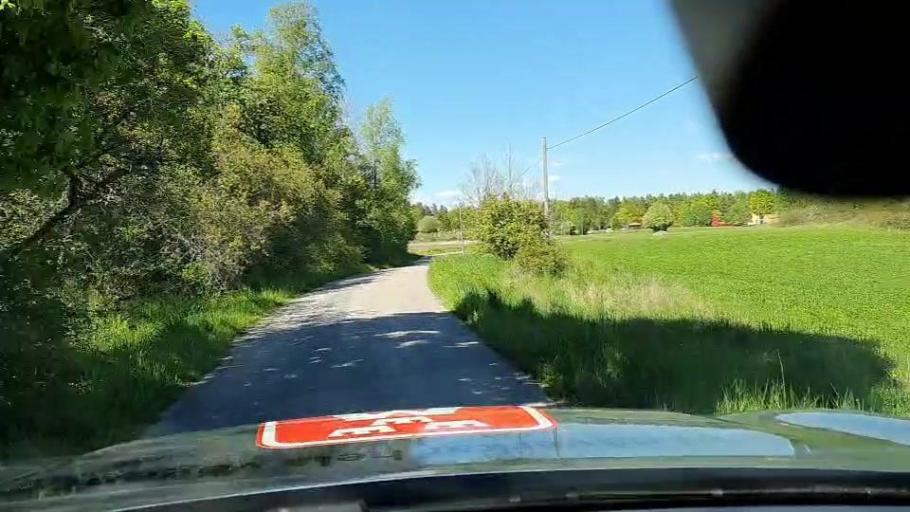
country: SE
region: Soedermanland
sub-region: Strangnas Kommun
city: Strangnas
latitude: 59.4549
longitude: 16.8787
